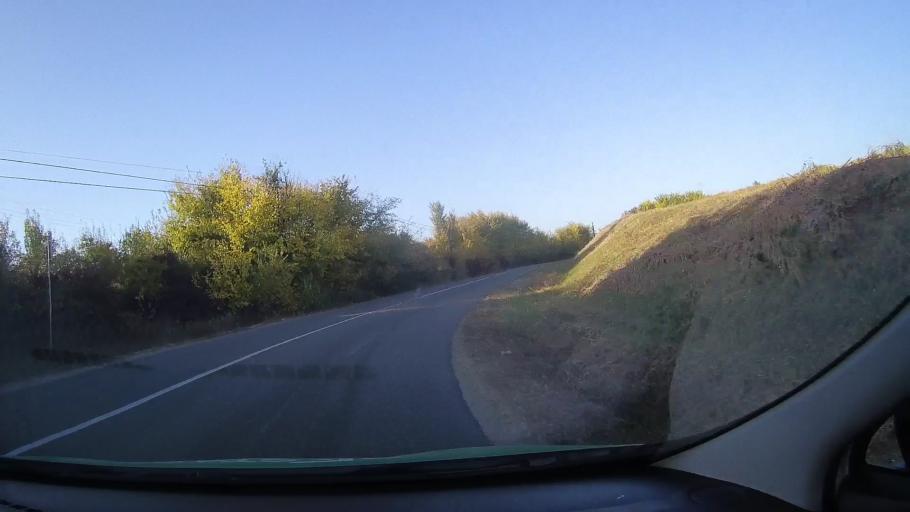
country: RO
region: Bihor
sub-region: Comuna Biharea
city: Oradea
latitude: 47.1001
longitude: 21.9262
